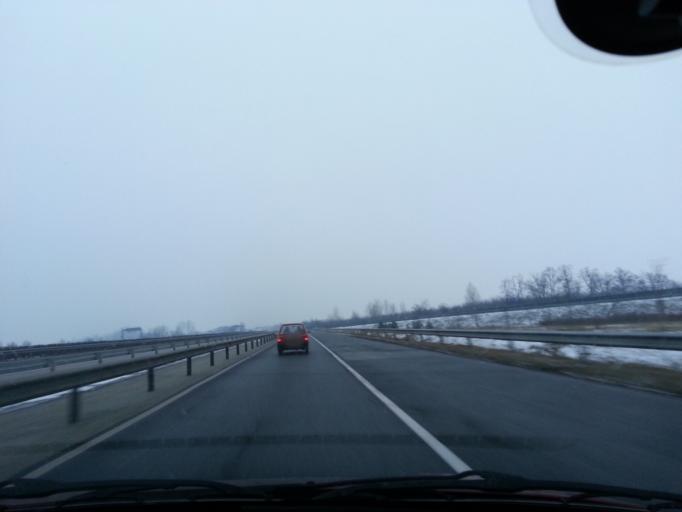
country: HU
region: Pest
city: Felsopakony
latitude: 47.3529
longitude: 19.2024
